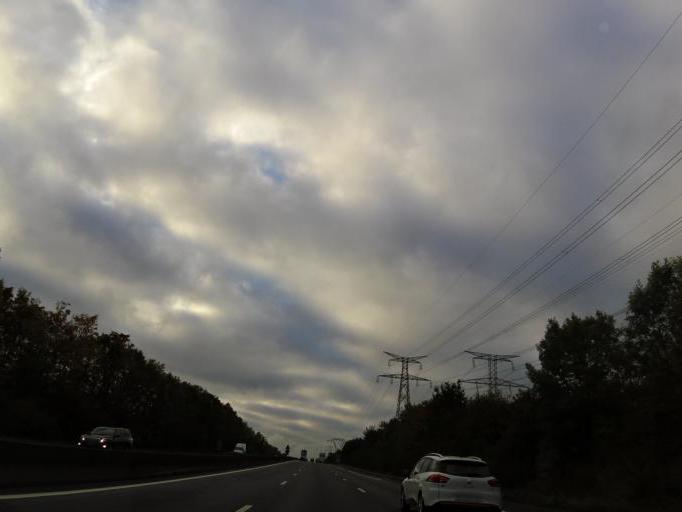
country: FR
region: Ile-de-France
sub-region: Departement de Seine-et-Marne
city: Torcy
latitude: 48.8490
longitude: 2.6613
